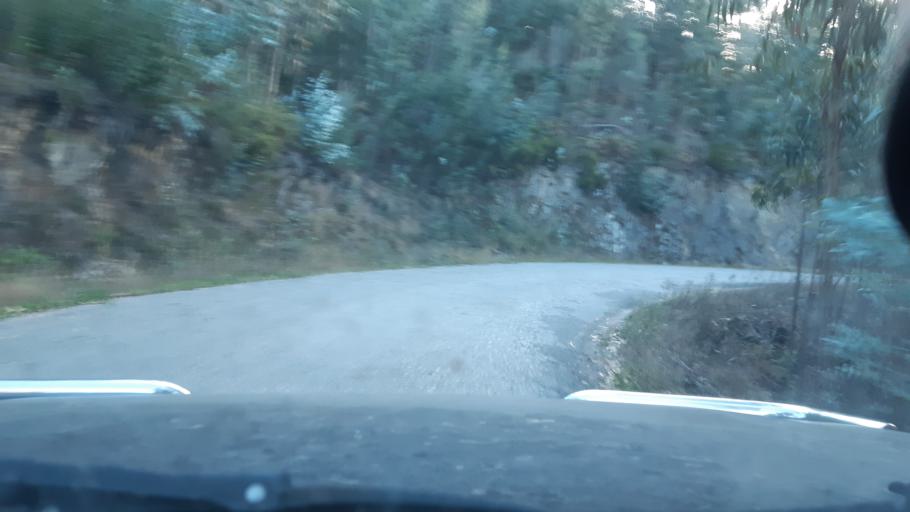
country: PT
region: Aveiro
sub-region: Agueda
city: Aguada de Cima
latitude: 40.5630
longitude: -8.3465
